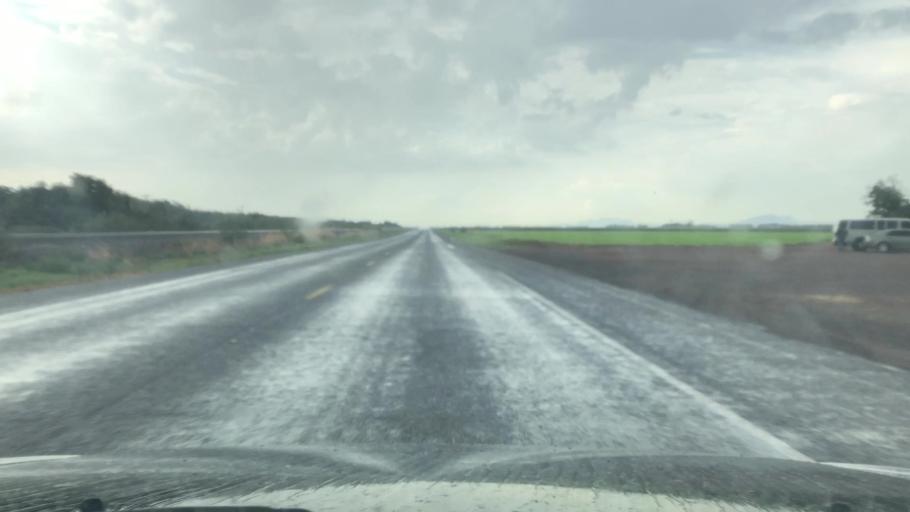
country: US
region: New Mexico
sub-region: Dona Ana County
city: Vado
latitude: 32.1345
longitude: -106.6776
